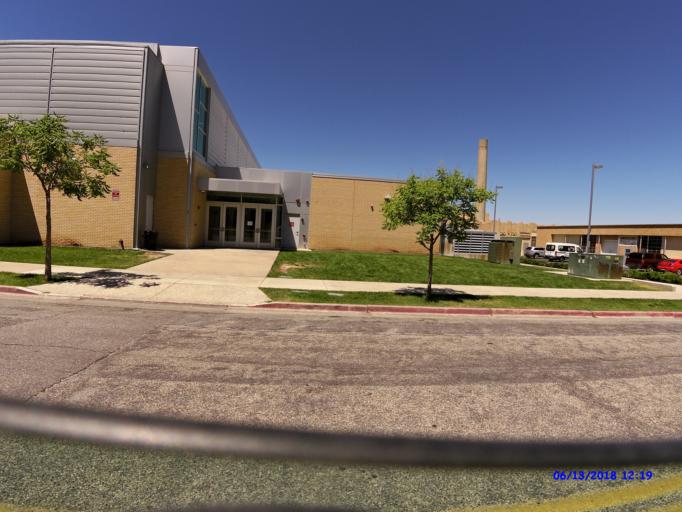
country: US
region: Utah
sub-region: Weber County
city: Ogden
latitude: 41.2127
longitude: -111.9456
